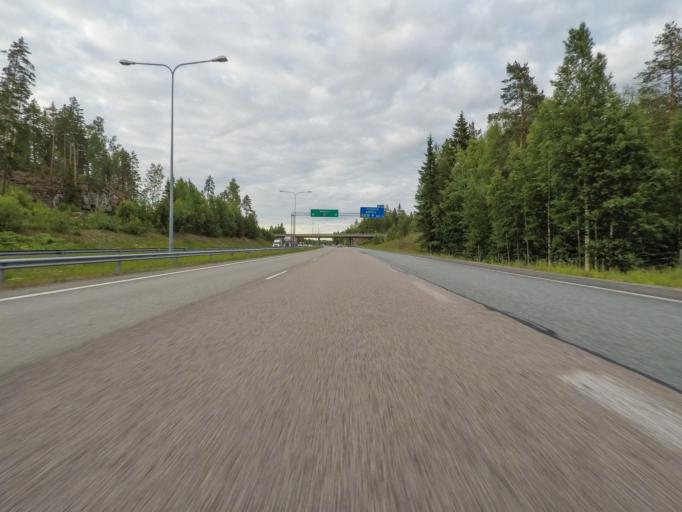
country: FI
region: Paijanne Tavastia
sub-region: Lahti
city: Heinola
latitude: 61.2784
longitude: 26.0685
